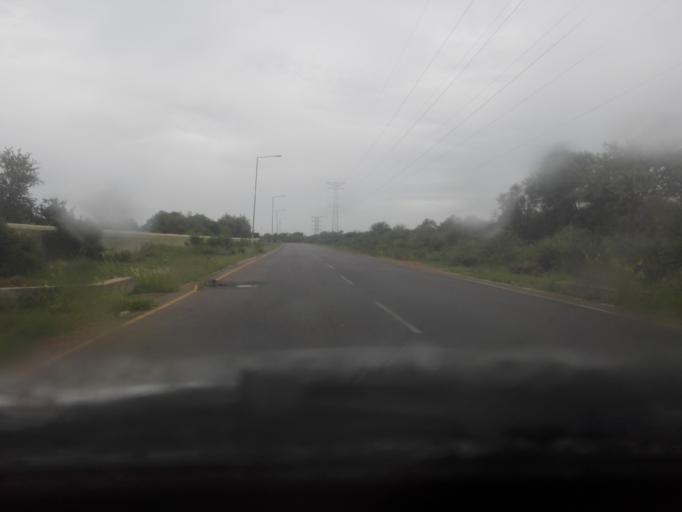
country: BW
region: South East
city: Gaborone
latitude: -24.6382
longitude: 25.8978
